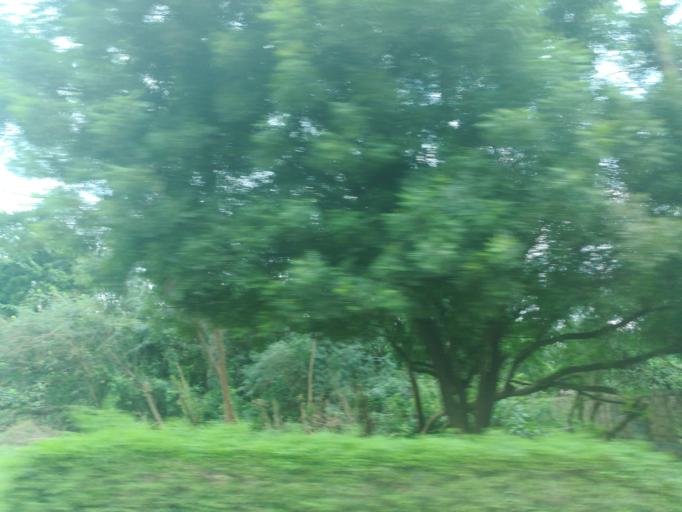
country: NG
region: Lagos
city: Ikorodu
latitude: 6.6432
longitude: 3.5237
